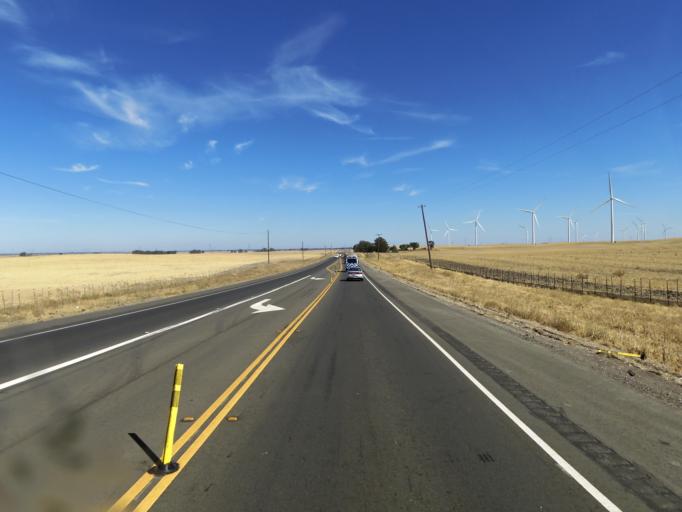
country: US
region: California
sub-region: Solano County
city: Rio Vista
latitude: 38.1835
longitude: -121.7782
